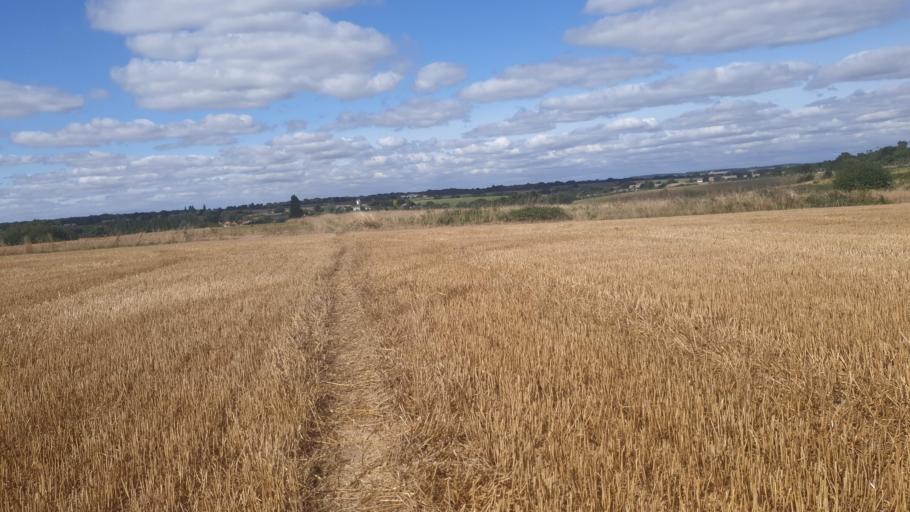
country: GB
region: England
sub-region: Essex
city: Dovercourt
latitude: 51.9201
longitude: 1.2197
